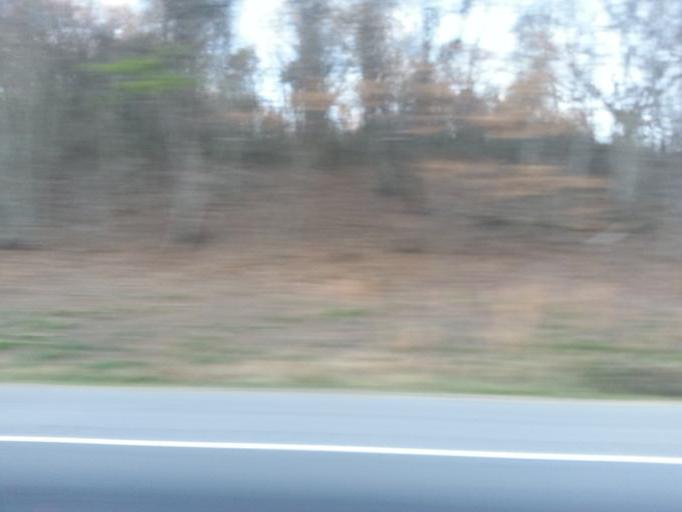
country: US
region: North Carolina
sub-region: Haywood County
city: Canton
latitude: 35.5501
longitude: -82.7367
